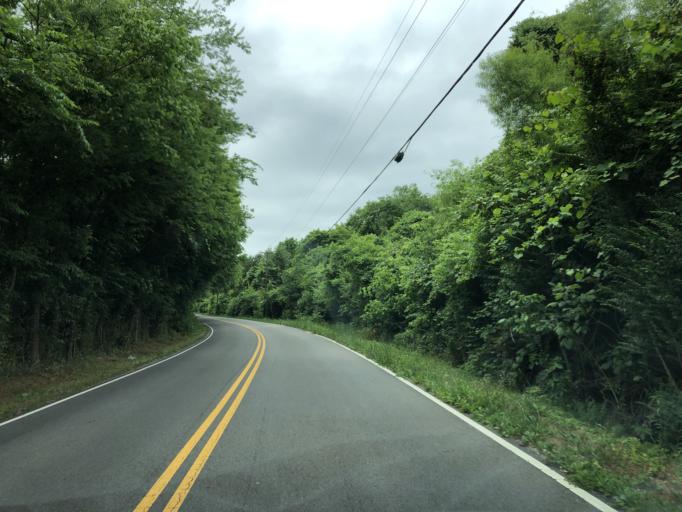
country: US
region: Tennessee
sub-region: Davidson County
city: Goodlettsville
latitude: 36.2953
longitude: -86.7818
